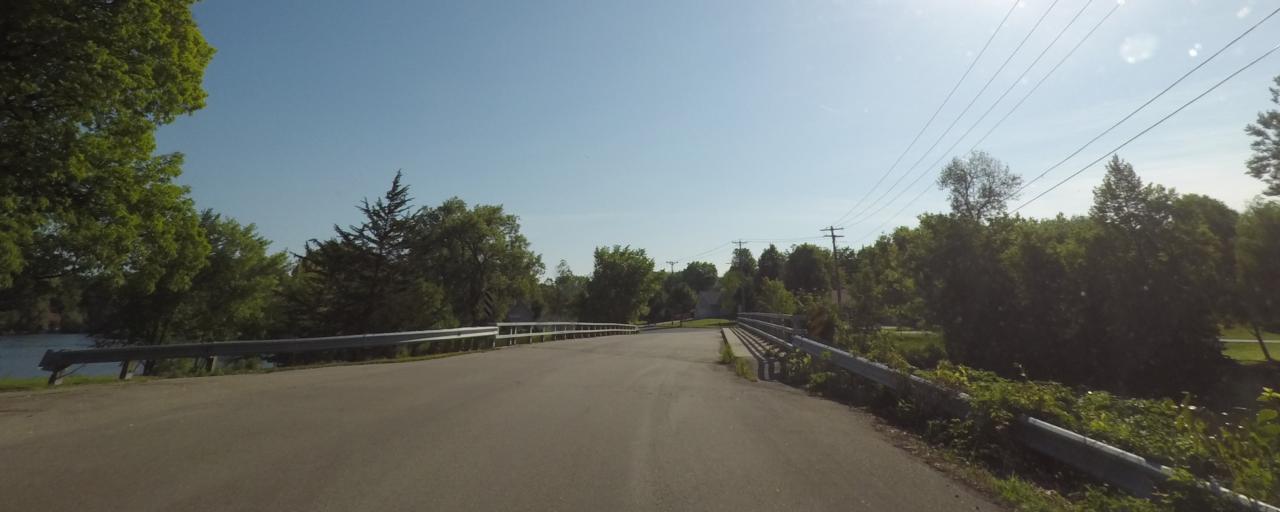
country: US
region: Wisconsin
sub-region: Dane County
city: McFarland
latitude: 43.0041
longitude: -89.3032
